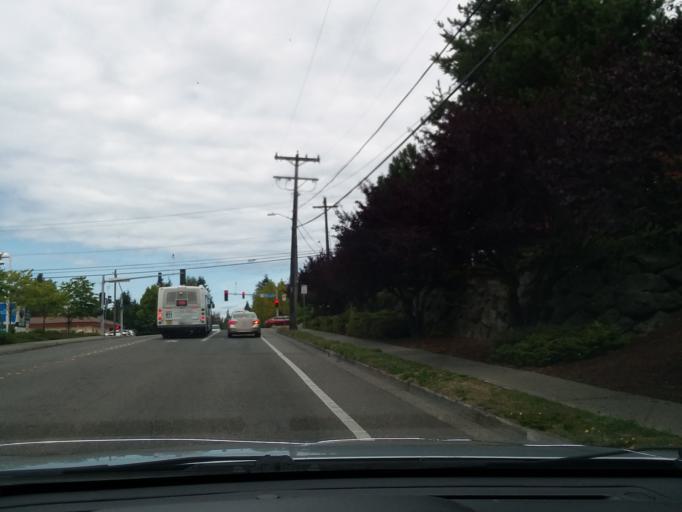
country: US
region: Washington
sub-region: Snohomish County
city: Alderwood Manor
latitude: 47.8203
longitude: -122.2978
